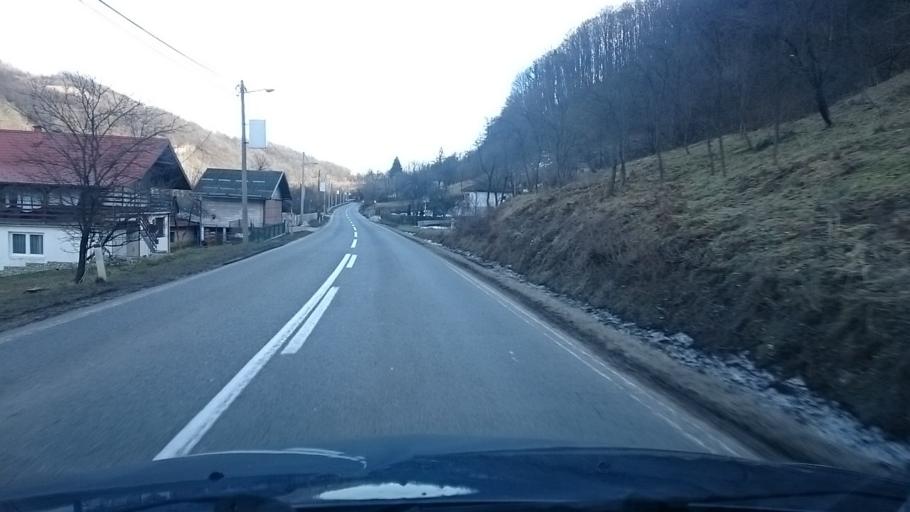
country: BA
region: Republika Srpska
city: Hiseti
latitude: 44.7215
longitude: 17.1580
